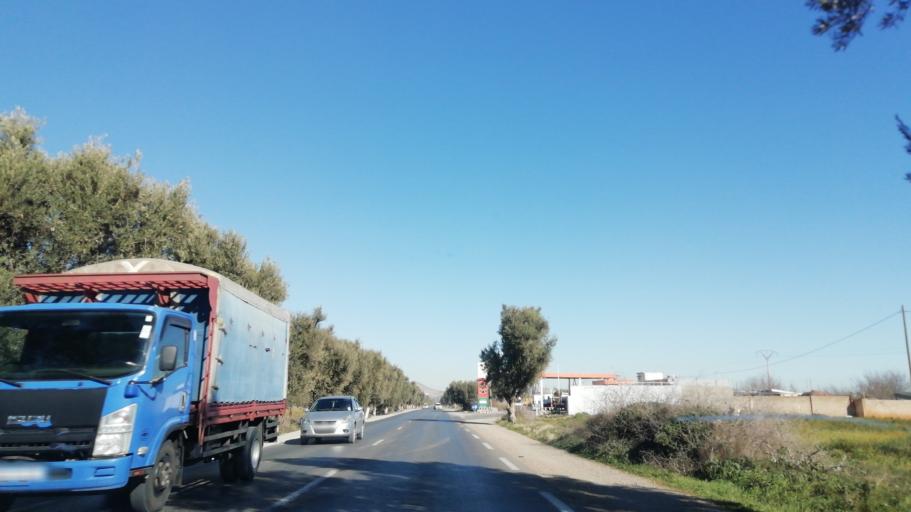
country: DZ
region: Mascara
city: Bou Hanifia el Hamamat
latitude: 35.1967
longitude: 0.1077
